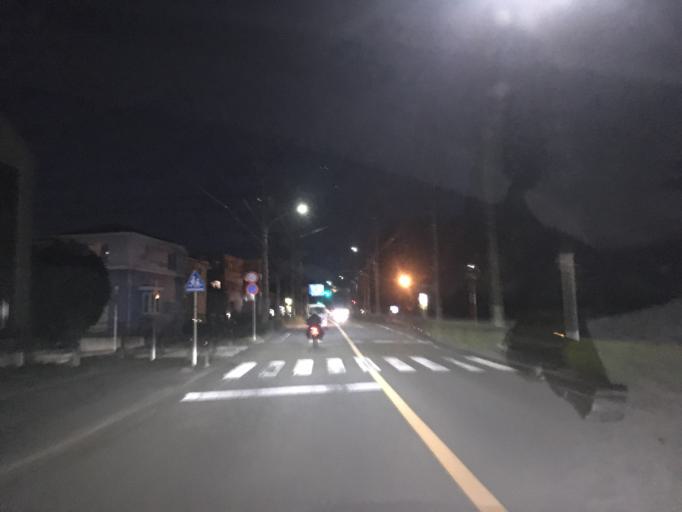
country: JP
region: Tokyo
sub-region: Machida-shi
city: Machida
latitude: 35.5849
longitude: 139.5177
